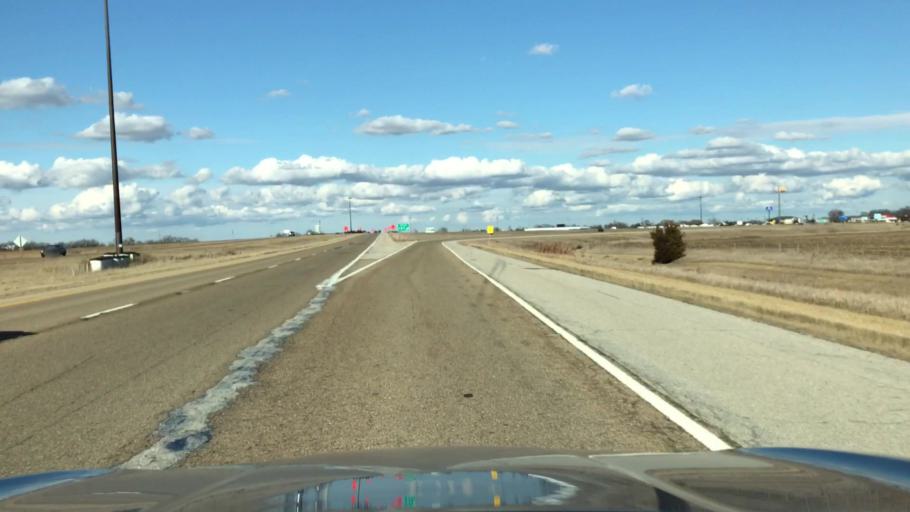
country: US
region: Illinois
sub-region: McLean County
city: Chenoa
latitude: 40.7357
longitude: -88.7373
